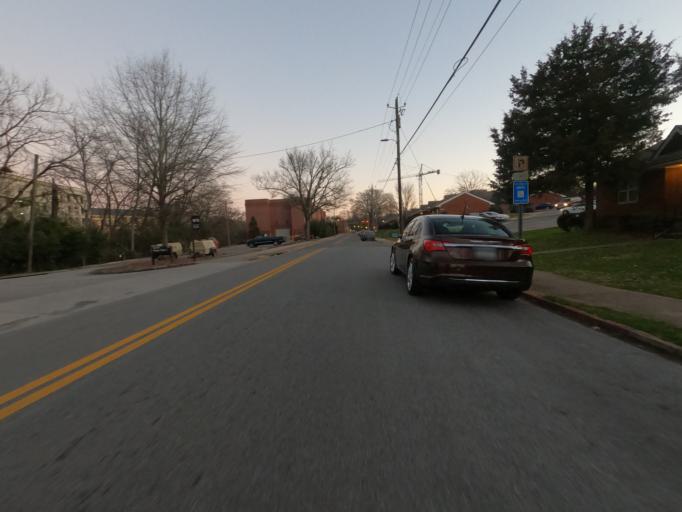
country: US
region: Georgia
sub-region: Clarke County
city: Athens
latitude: 33.9530
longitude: -83.3799
